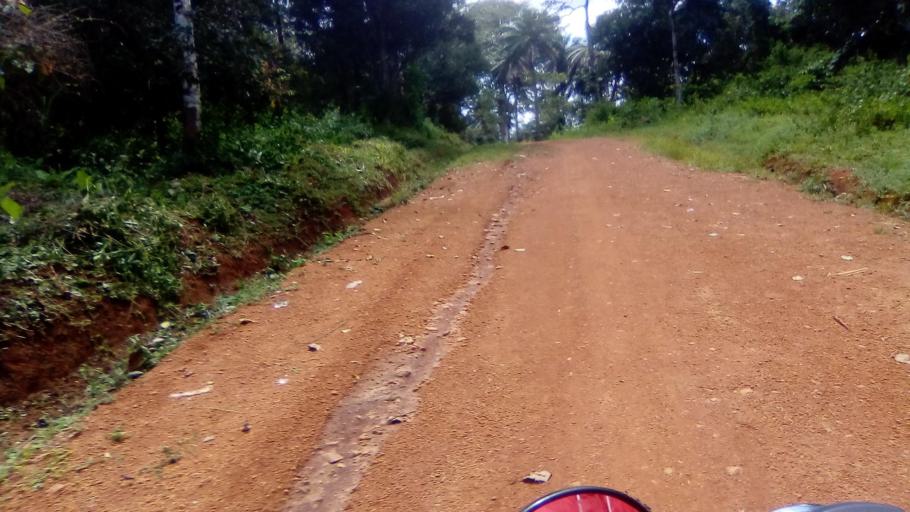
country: SL
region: Eastern Province
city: Giehun
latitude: 8.5051
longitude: -10.9044
